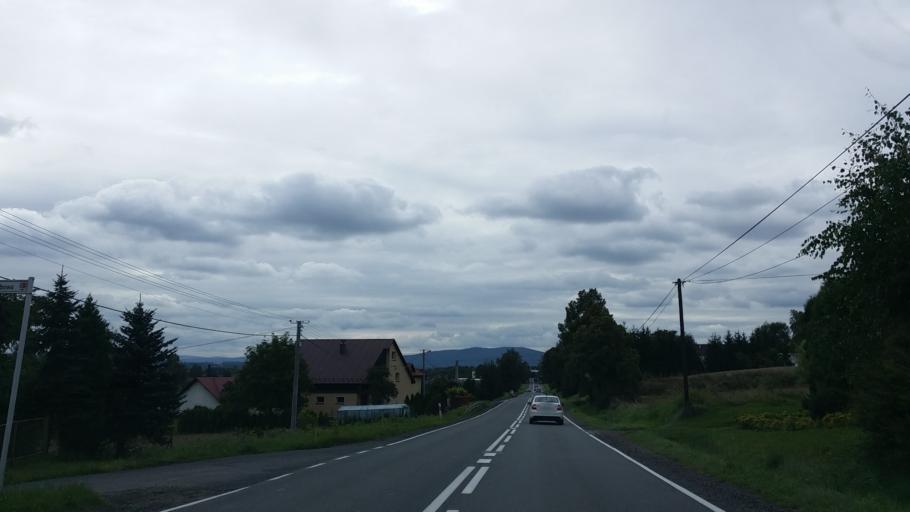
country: PL
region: Lesser Poland Voivodeship
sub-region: Powiat wadowicki
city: Radocza
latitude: 49.9226
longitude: 19.4783
